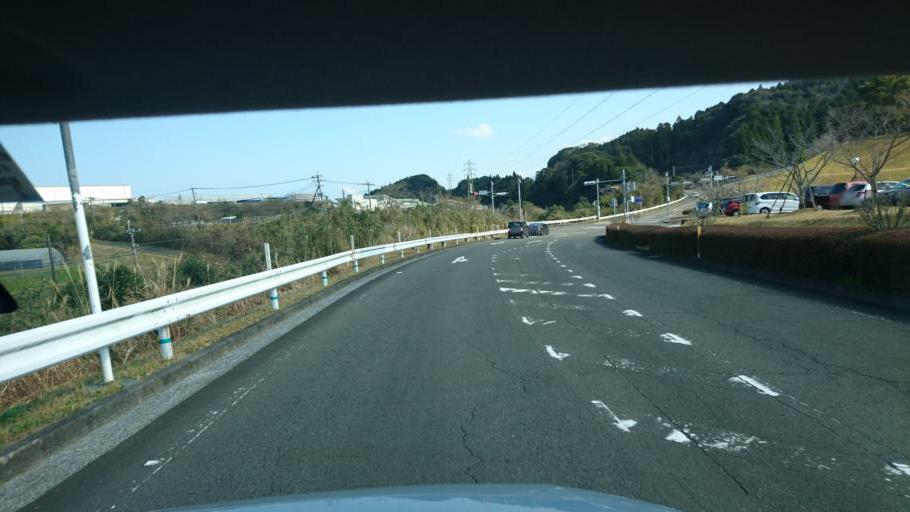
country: JP
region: Miyazaki
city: Miyazaki-shi
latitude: 31.8364
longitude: 131.4007
